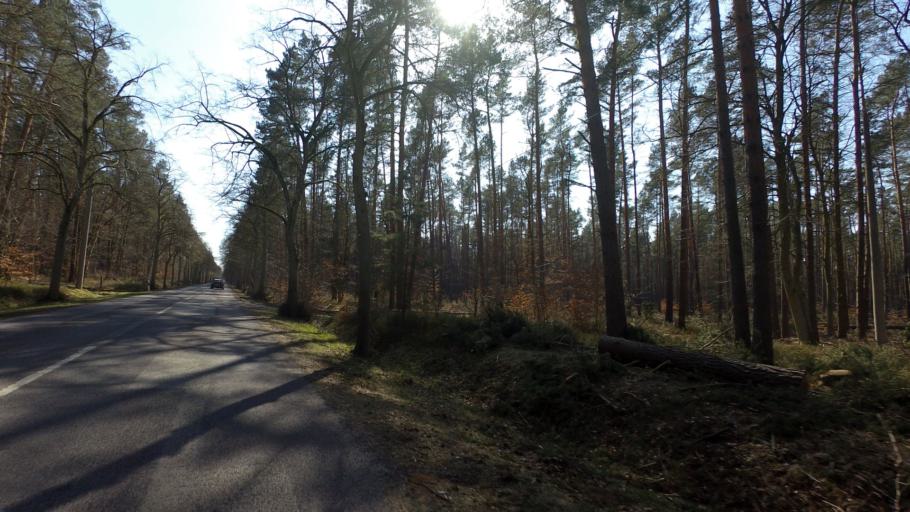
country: DE
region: Brandenburg
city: Leegebruch
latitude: 52.7891
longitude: 13.1678
